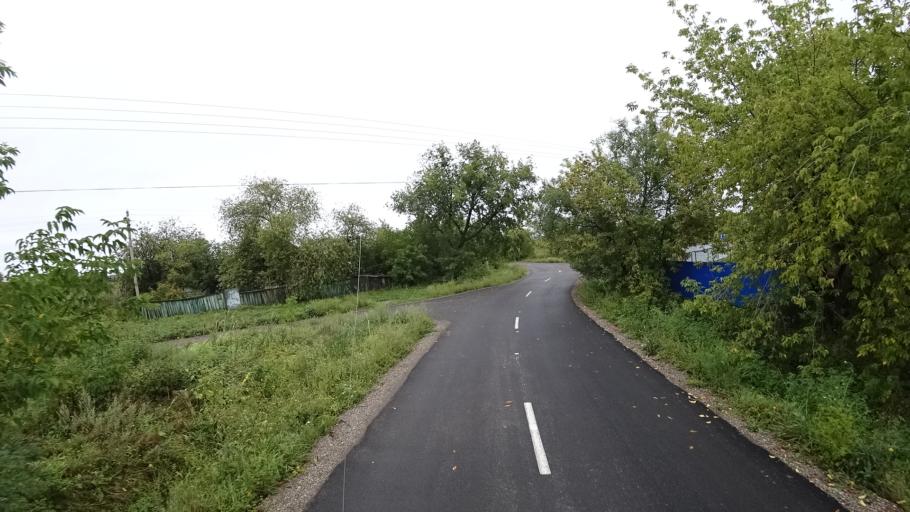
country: RU
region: Primorskiy
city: Monastyrishche
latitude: 44.1966
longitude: 132.4973
